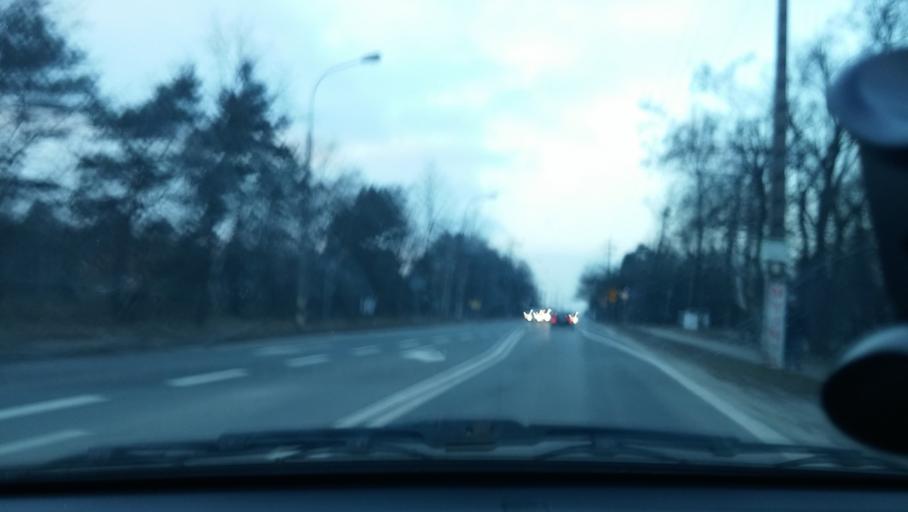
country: PL
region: Masovian Voivodeship
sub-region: Warszawa
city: Wawer
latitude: 52.1871
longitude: 21.1865
